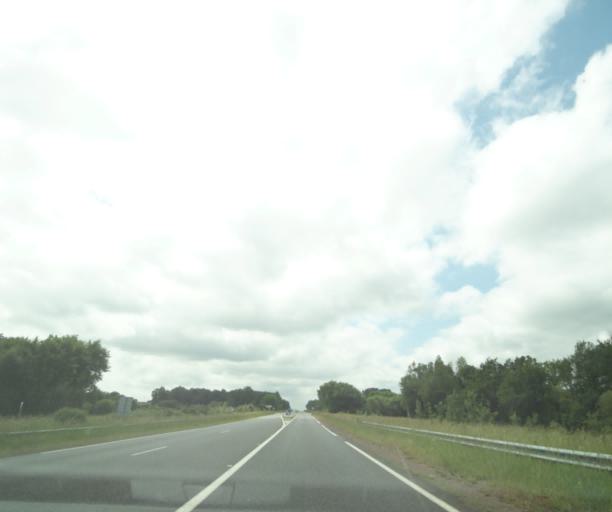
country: FR
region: Poitou-Charentes
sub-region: Departement des Deux-Sevres
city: Airvault
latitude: 46.7999
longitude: -0.2127
